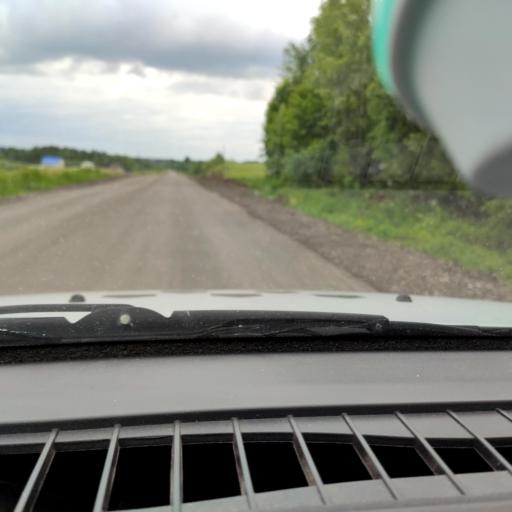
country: RU
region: Perm
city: Uinskoye
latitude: 57.1724
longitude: 56.5626
